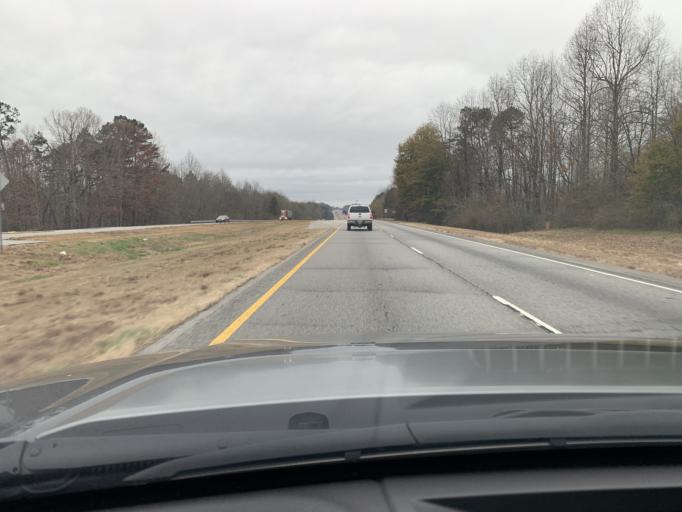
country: US
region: Georgia
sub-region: Hall County
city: Lula
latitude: 34.4087
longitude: -83.6695
